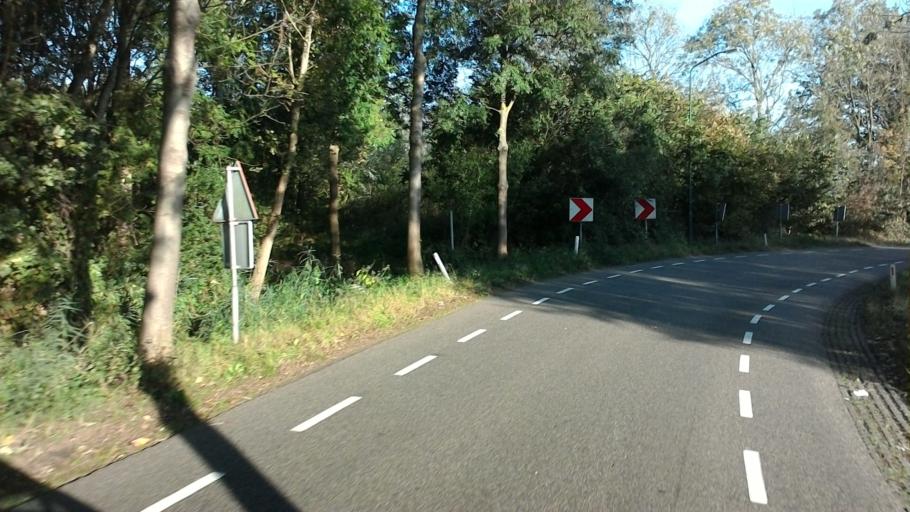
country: NL
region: North Brabant
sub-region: Gemeente Schijndel
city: Schijndel
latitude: 51.6268
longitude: 5.4401
